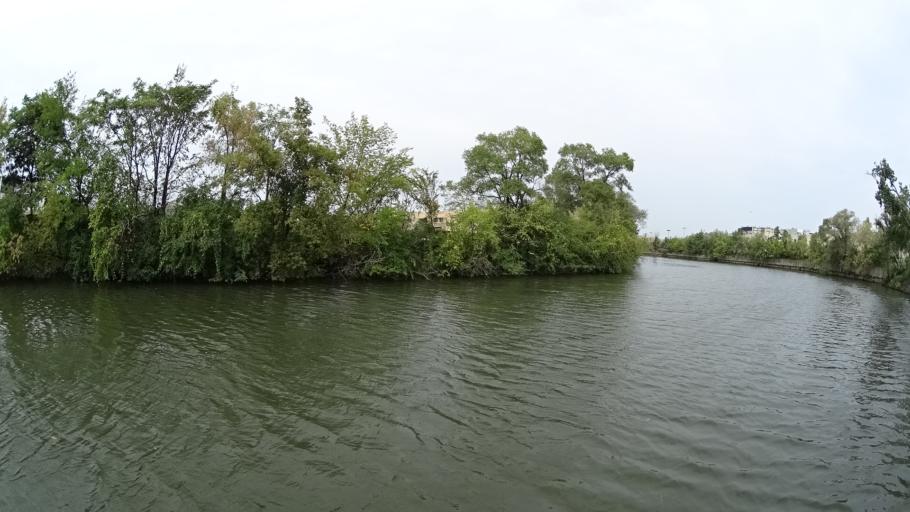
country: US
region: Illinois
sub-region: Cook County
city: Chicago
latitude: 41.9256
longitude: -87.6744
